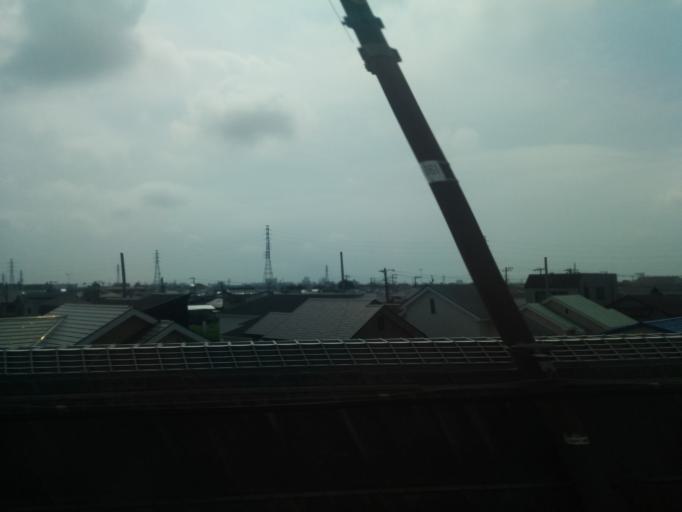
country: JP
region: Kanagawa
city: Hiratsuka
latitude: 35.3520
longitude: 139.3167
